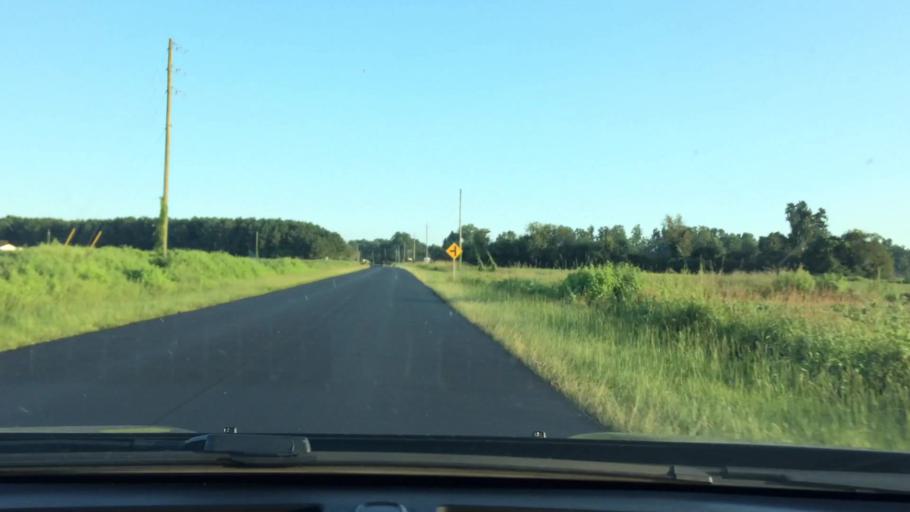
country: US
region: North Carolina
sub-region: Pitt County
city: Ayden
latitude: 35.4340
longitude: -77.4510
